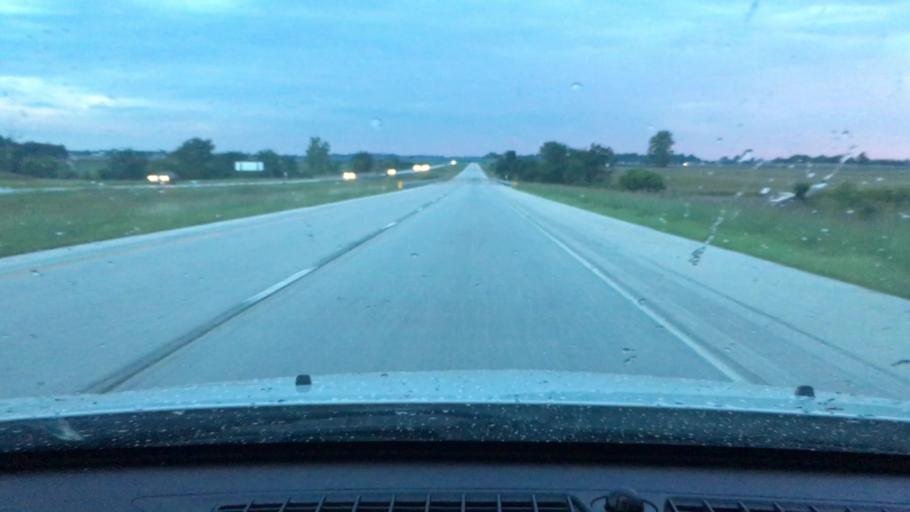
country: US
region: Illinois
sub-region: Morgan County
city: South Jacksonville
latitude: 39.7061
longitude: -90.1852
